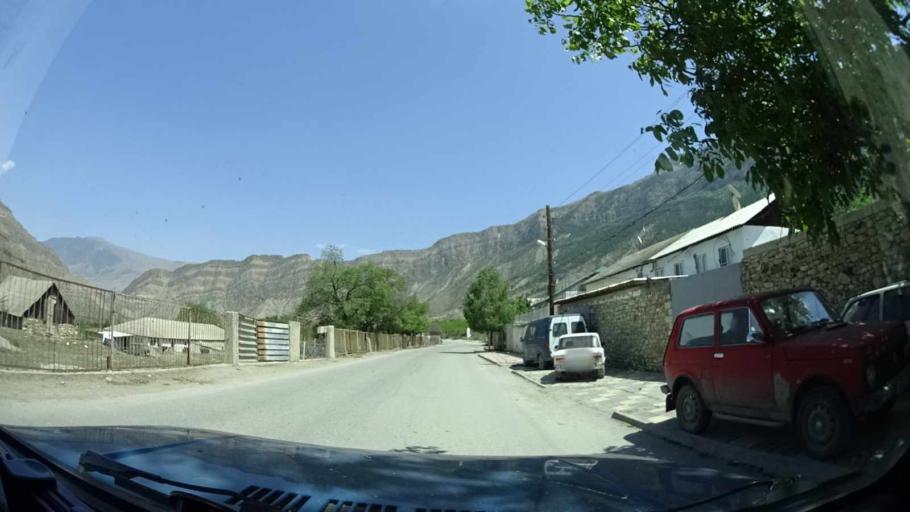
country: RU
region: Dagestan
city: Gergebil'
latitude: 42.4691
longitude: 47.0437
